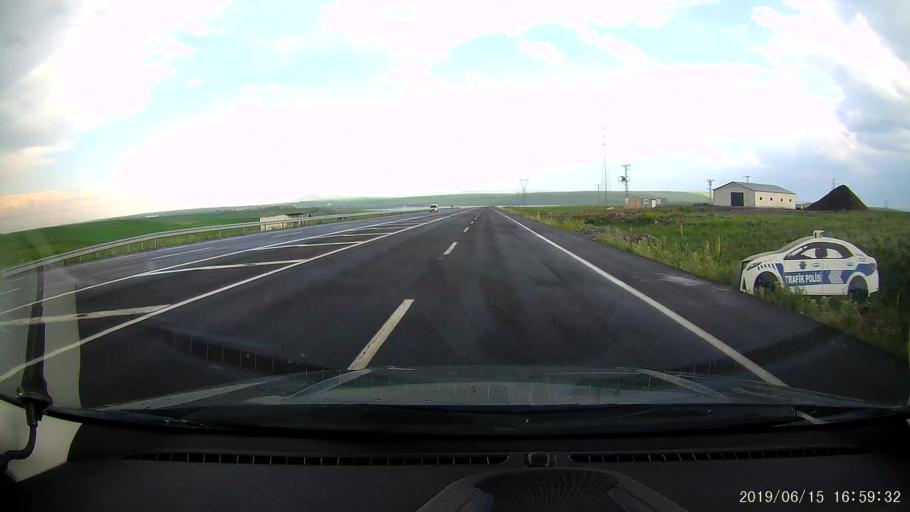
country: TR
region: Kars
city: Susuz
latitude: 40.7506
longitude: 43.1514
